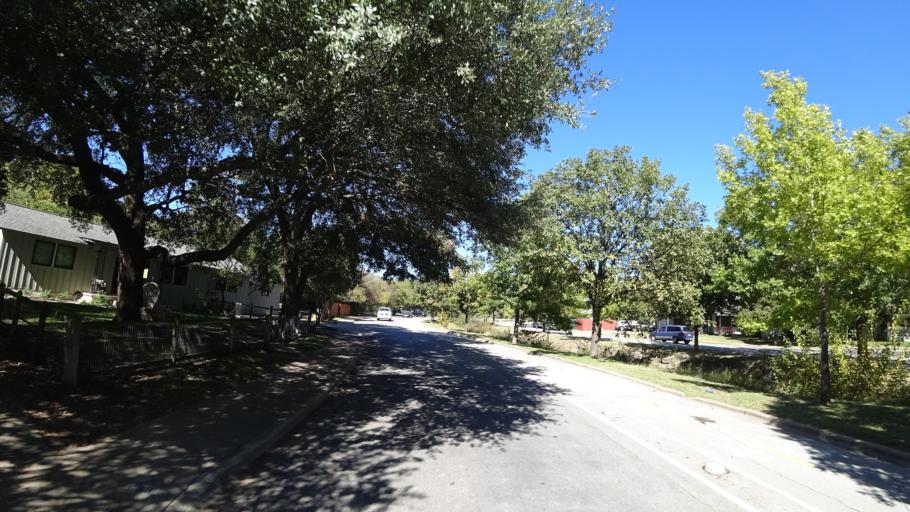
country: US
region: Texas
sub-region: Travis County
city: Austin
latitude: 30.3360
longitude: -97.7326
